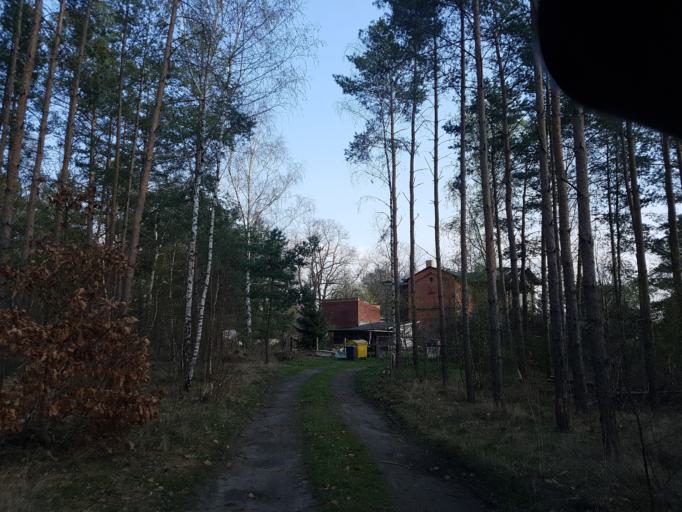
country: DE
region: Brandenburg
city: Schonborn
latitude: 51.6027
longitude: 13.4663
